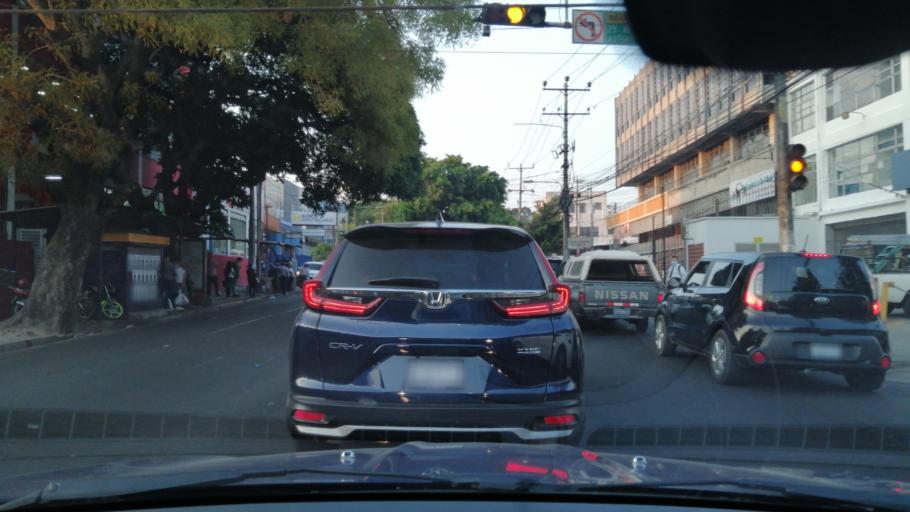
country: SV
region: San Salvador
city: San Salvador
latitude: 13.7127
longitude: -89.2036
